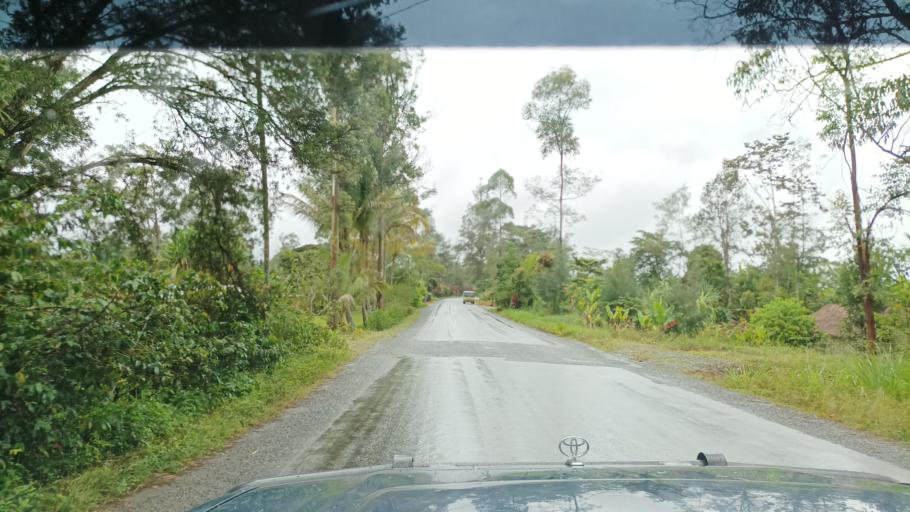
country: PG
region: Jiwaka
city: Minj
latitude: -5.8417
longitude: 144.6120
